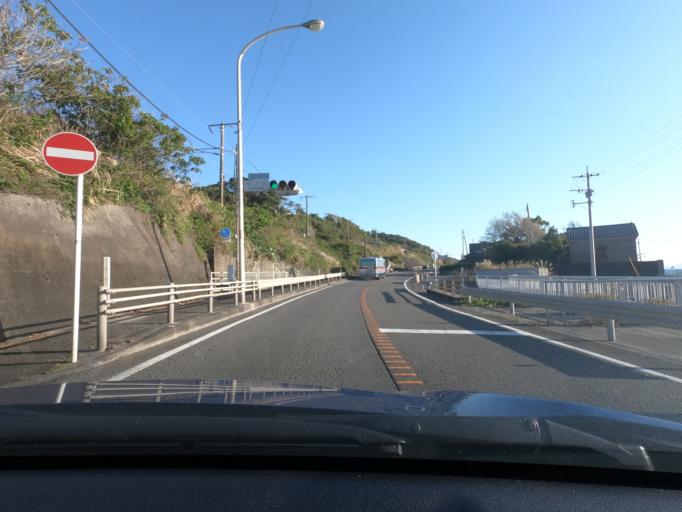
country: JP
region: Kagoshima
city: Akune
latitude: 31.9721
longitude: 130.2096
